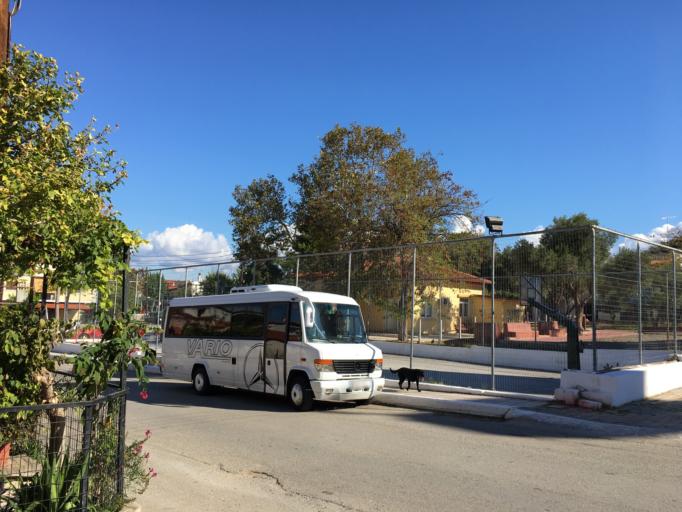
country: GR
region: Central Macedonia
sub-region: Nomos Chalkidikis
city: Nea Poteidaia
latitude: 40.1933
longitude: 23.3275
